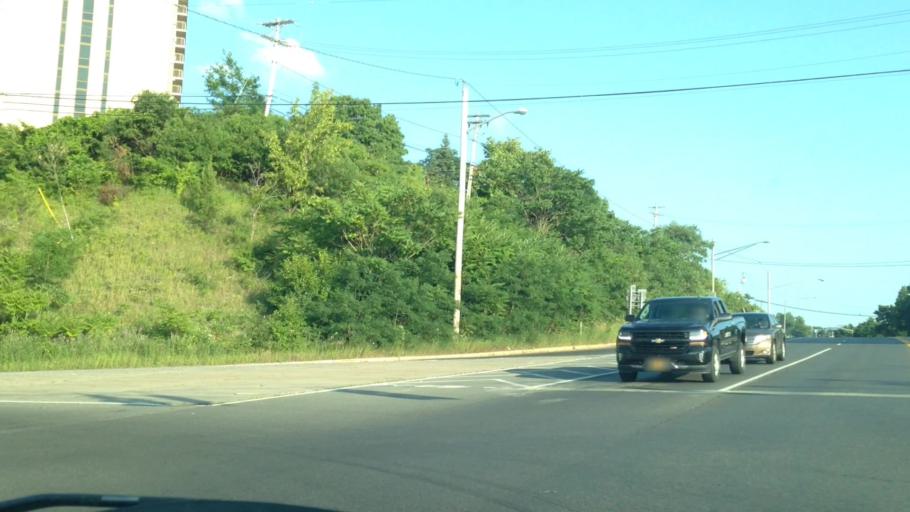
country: US
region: New York
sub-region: Onondaga County
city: Nedrow
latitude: 43.0060
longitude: -76.1315
